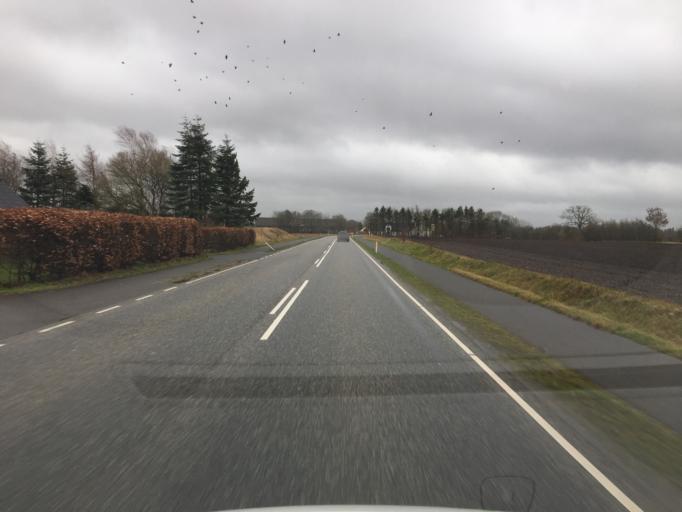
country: DK
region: South Denmark
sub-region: Aabenraa Kommune
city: Tinglev
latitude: 54.9243
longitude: 9.2456
